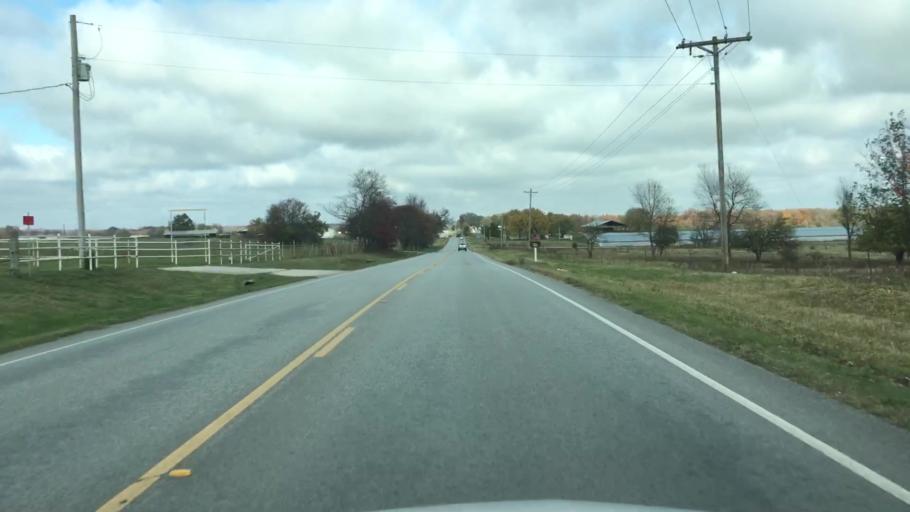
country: US
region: Arkansas
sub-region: Benton County
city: Centerton
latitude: 36.2694
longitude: -94.3503
